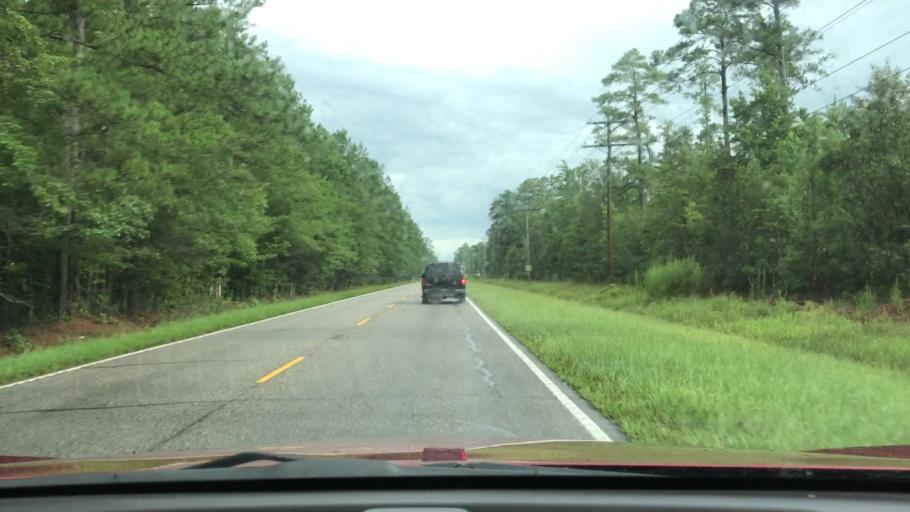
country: US
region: South Carolina
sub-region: Georgetown County
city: Georgetown
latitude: 33.4479
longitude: -79.2786
